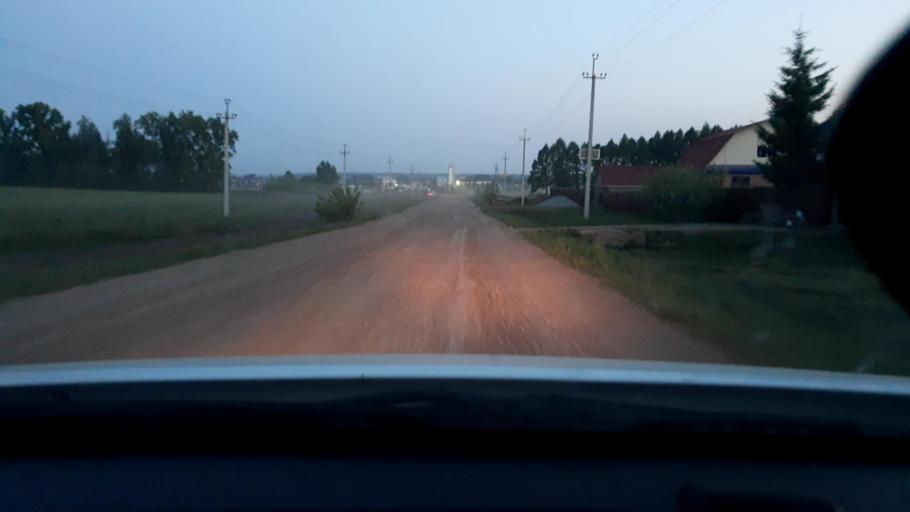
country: RU
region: Bashkortostan
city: Avdon
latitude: 54.5148
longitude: 55.8224
